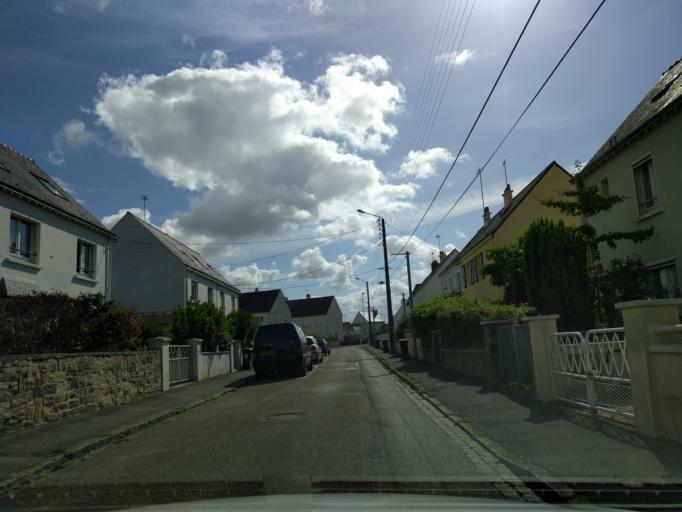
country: FR
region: Brittany
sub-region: Departement du Morbihan
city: Lorient
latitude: 47.7407
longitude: -3.3916
